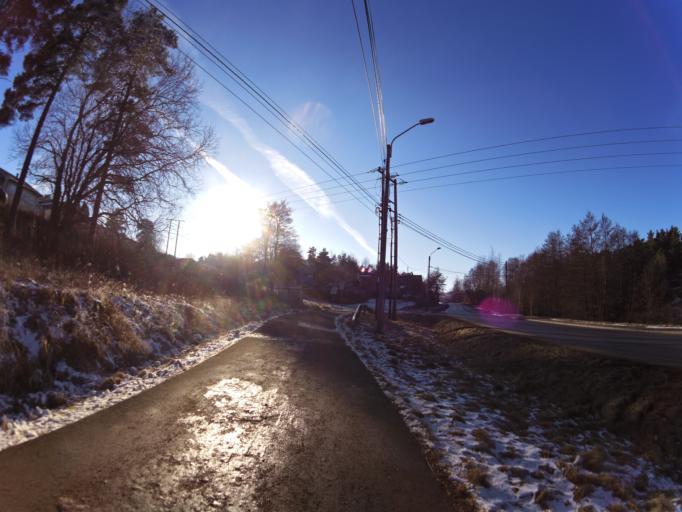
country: NO
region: Ostfold
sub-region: Fredrikstad
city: Fredrikstad
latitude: 59.2031
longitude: 10.8798
